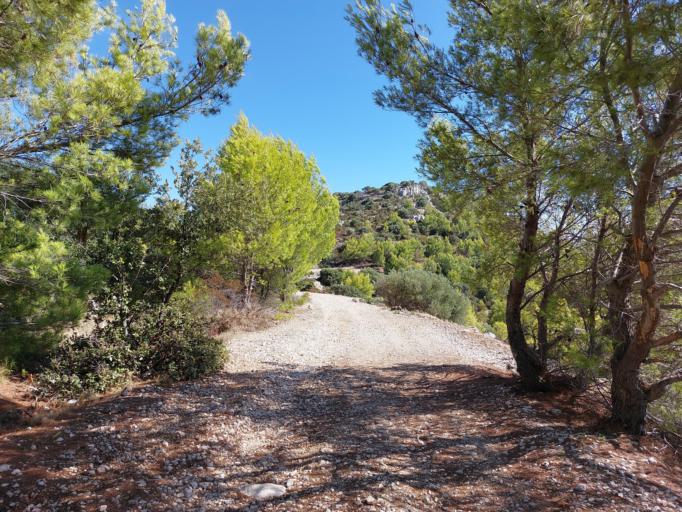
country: HR
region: Dubrovacko-Neretvanska
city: Smokvica
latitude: 42.7308
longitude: 16.8404
